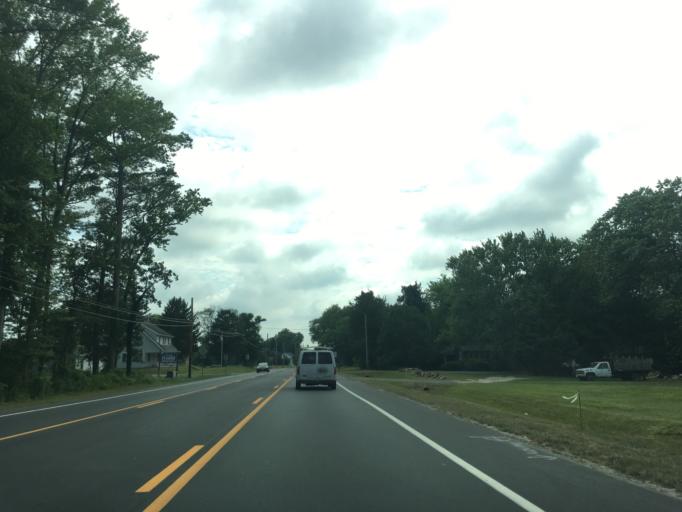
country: US
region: Delaware
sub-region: Sussex County
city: Ocean View
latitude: 38.5512
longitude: -75.1431
